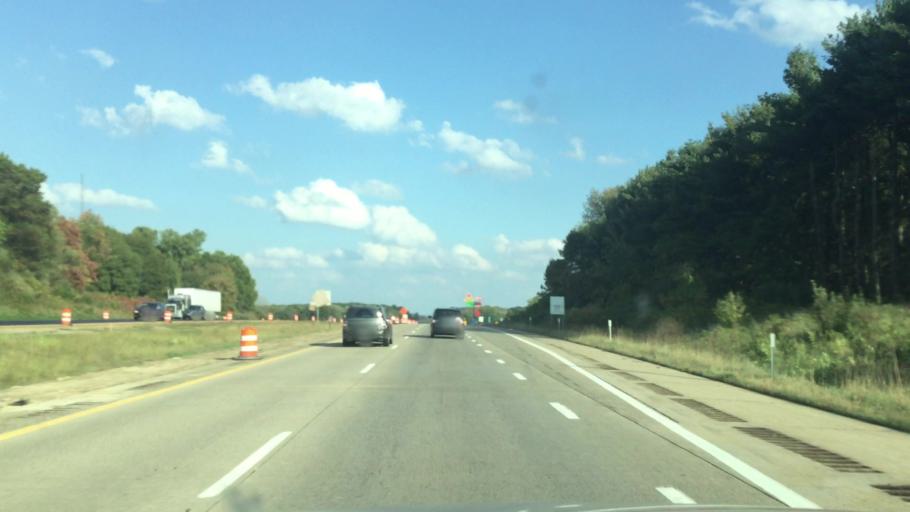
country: US
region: Michigan
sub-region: Calhoun County
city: Marshall
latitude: 42.2822
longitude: -84.9360
